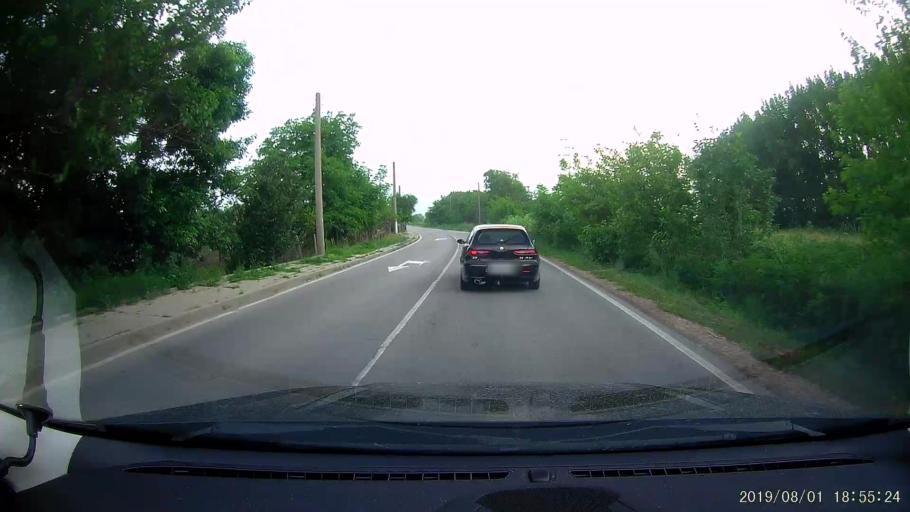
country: BG
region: Shumen
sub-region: Obshtina Smyadovo
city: Smyadovo
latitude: 43.1814
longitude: 27.0057
